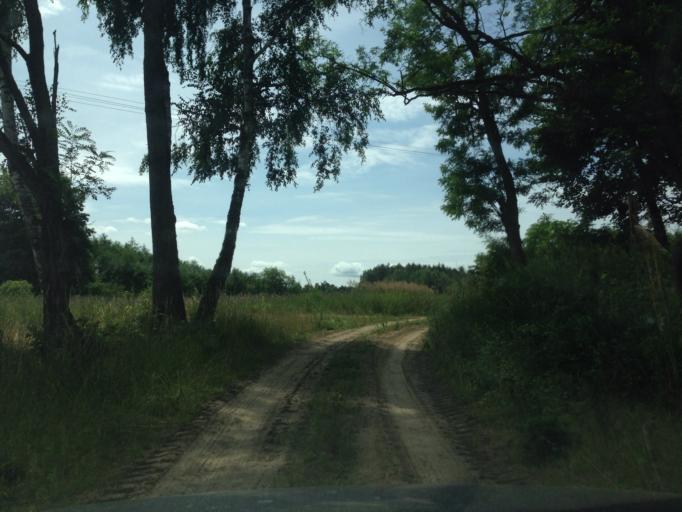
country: PL
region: Kujawsko-Pomorskie
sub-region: Powiat brodnicki
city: Bartniczka
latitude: 53.2674
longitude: 19.5853
